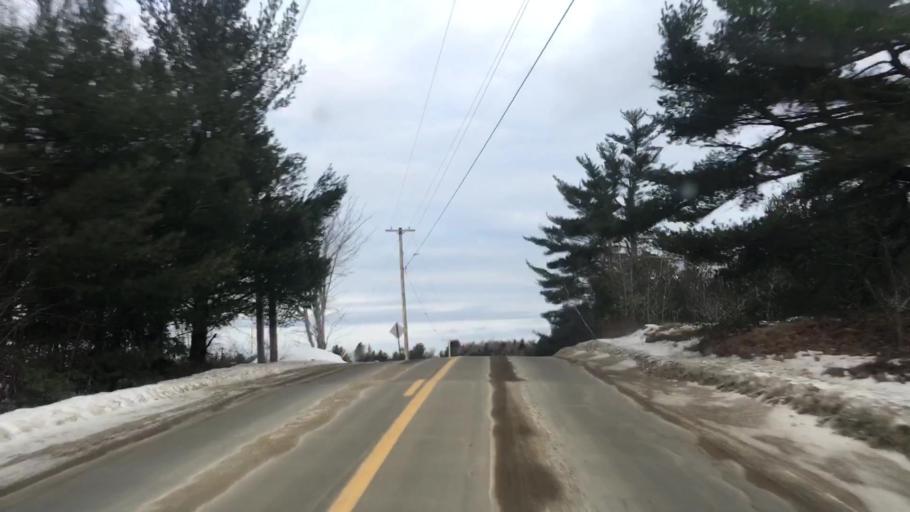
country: US
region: Maine
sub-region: Hancock County
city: Franklin
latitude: 44.8379
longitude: -68.3224
